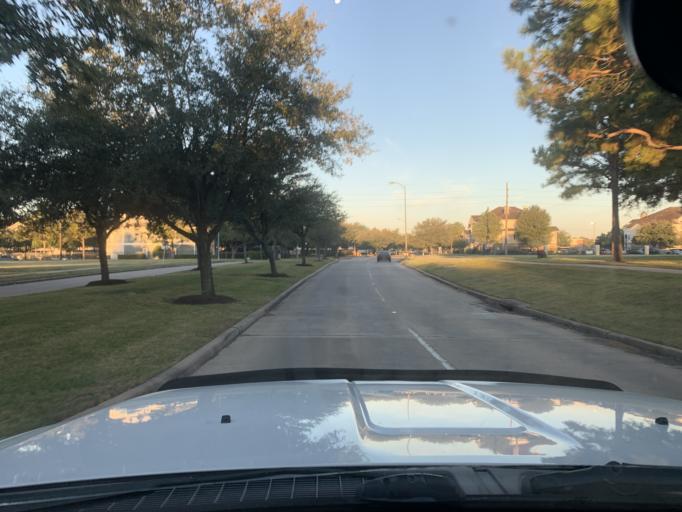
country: US
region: Texas
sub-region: Fort Bend County
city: Four Corners
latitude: 29.6482
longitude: -95.6467
